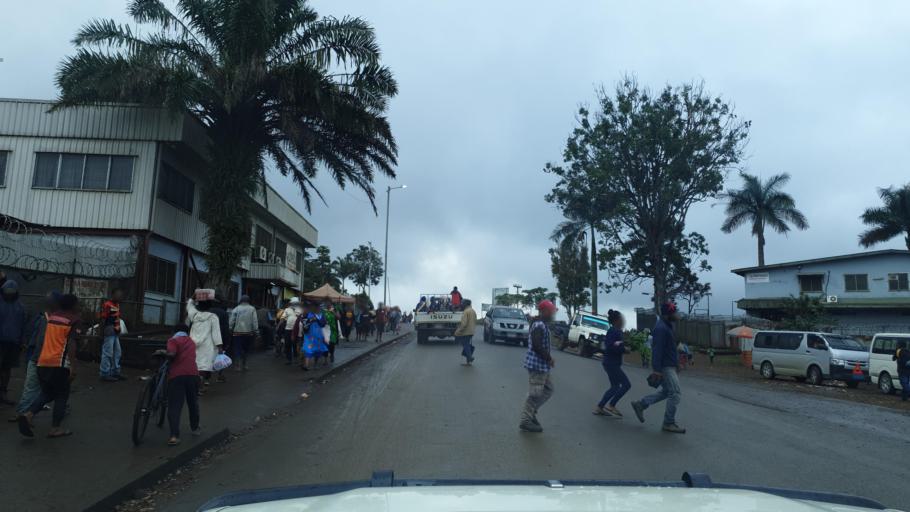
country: PG
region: Eastern Highlands
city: Goroka
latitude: -6.0726
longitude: 145.3904
